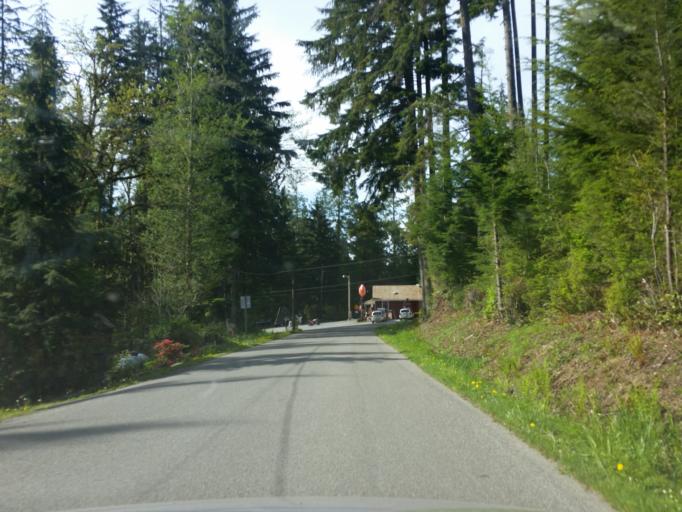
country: US
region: Washington
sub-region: Snohomish County
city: Woods Creek
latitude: 47.9887
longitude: -121.9035
